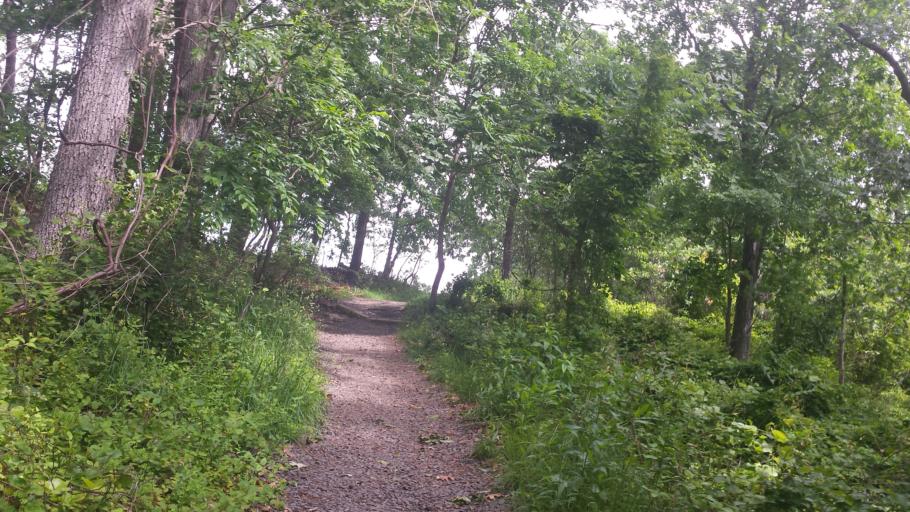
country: US
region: New York
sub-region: Westchester County
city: Harrison
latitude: 40.9504
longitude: -73.7019
